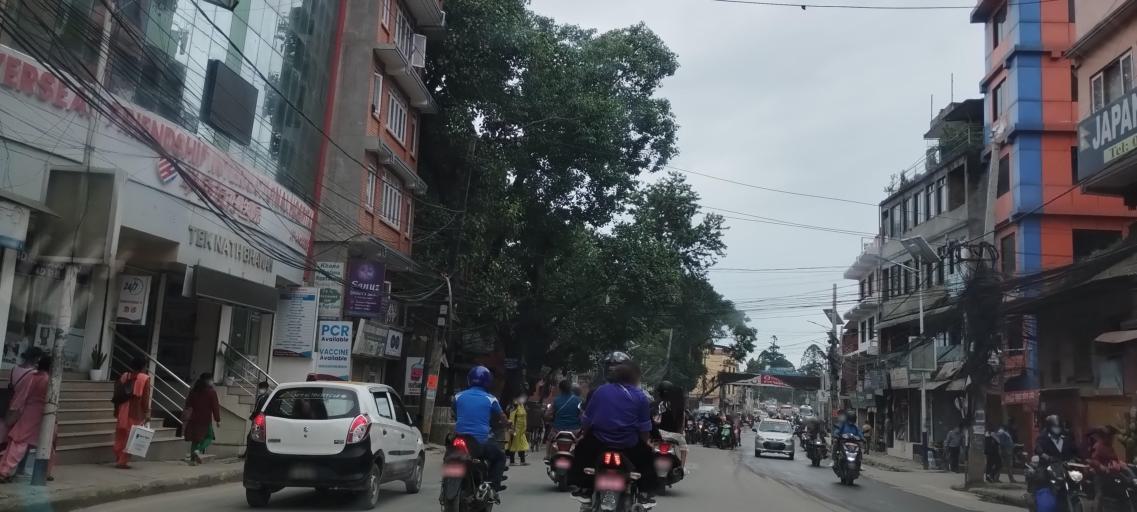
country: NP
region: Central Region
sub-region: Bagmati Zone
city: Kathmandu
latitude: 27.7183
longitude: 85.3117
